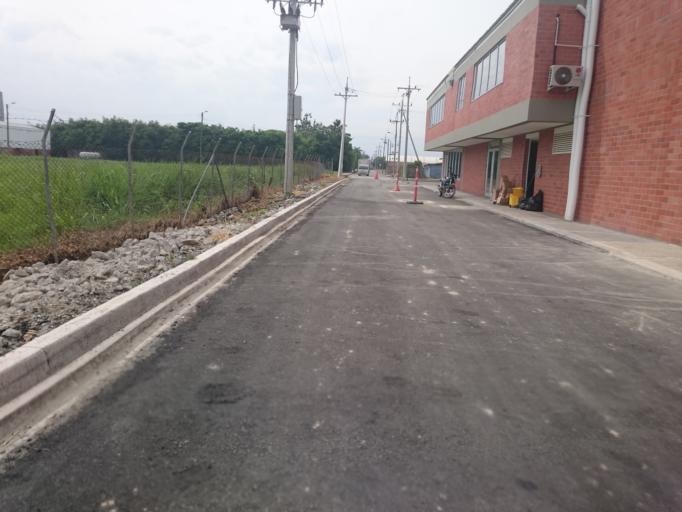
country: CO
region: Cauca
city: Puerto Tejada
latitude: 3.2107
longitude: -76.4266
